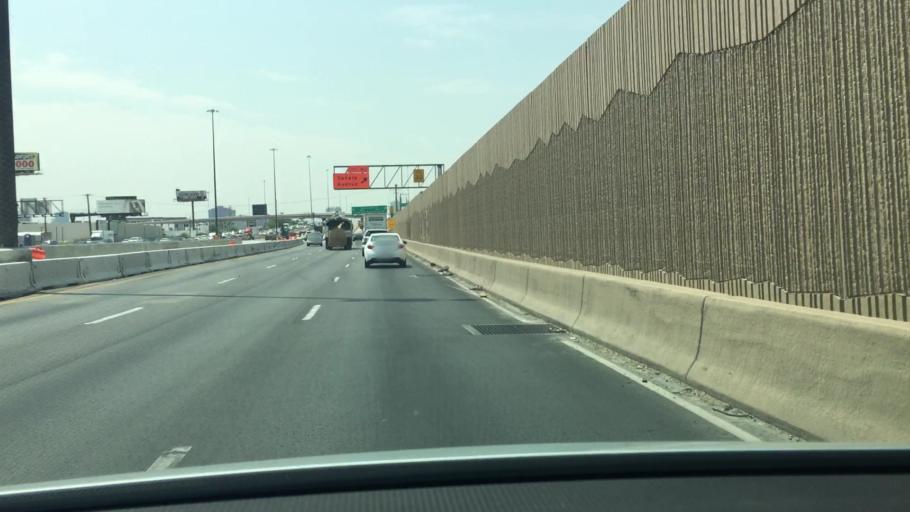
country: US
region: Nevada
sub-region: Clark County
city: Las Vegas
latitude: 36.1505
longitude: -115.1665
